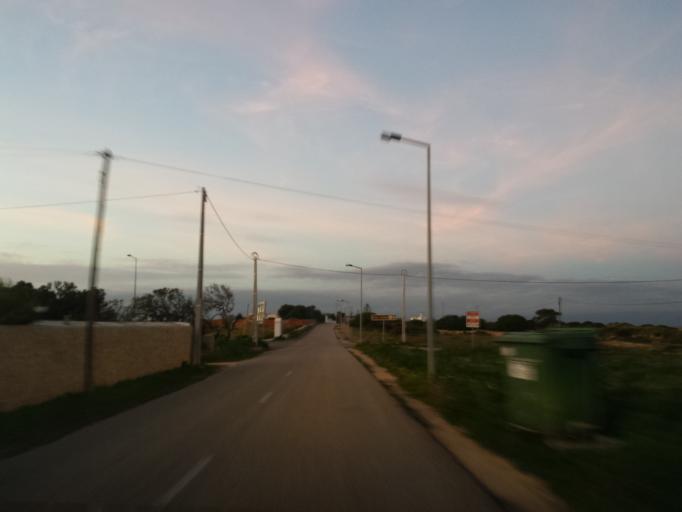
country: PT
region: Faro
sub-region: Lagos
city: Lagos
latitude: 37.0860
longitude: -8.6709
